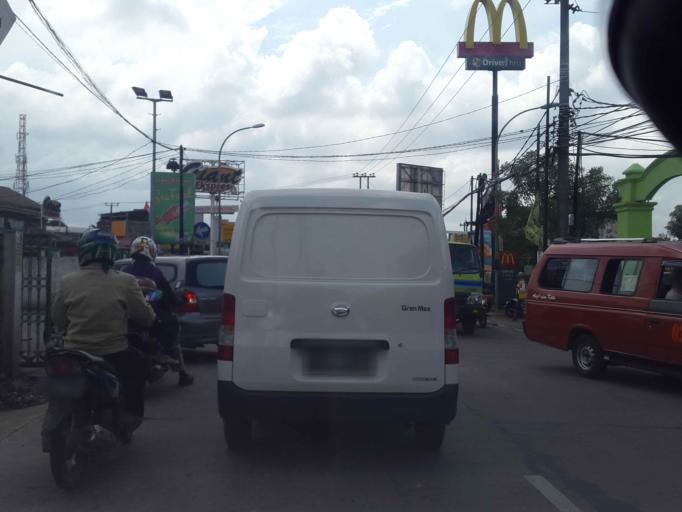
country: ID
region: West Java
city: Bekasi
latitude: -6.2695
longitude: 106.9818
